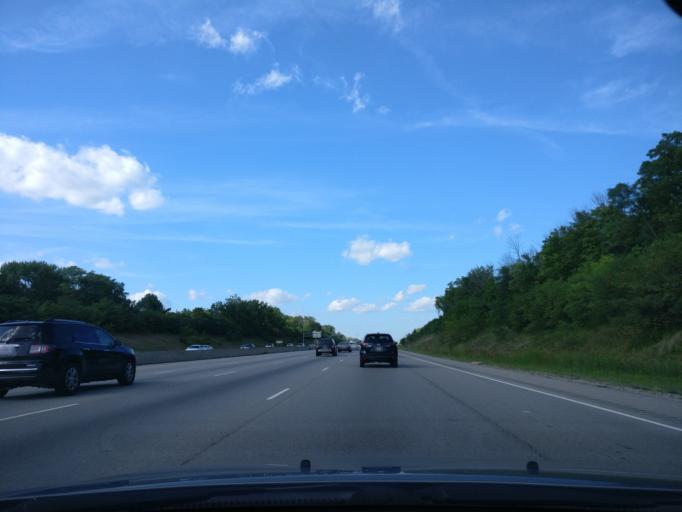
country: US
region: Ohio
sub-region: Warren County
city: Hunter
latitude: 39.5020
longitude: -84.3232
